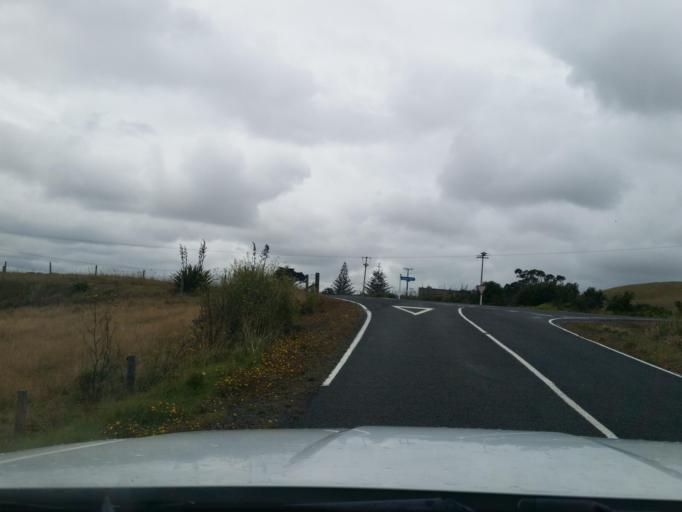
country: NZ
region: Northland
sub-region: Kaipara District
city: Dargaville
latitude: -35.9983
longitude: 173.7999
